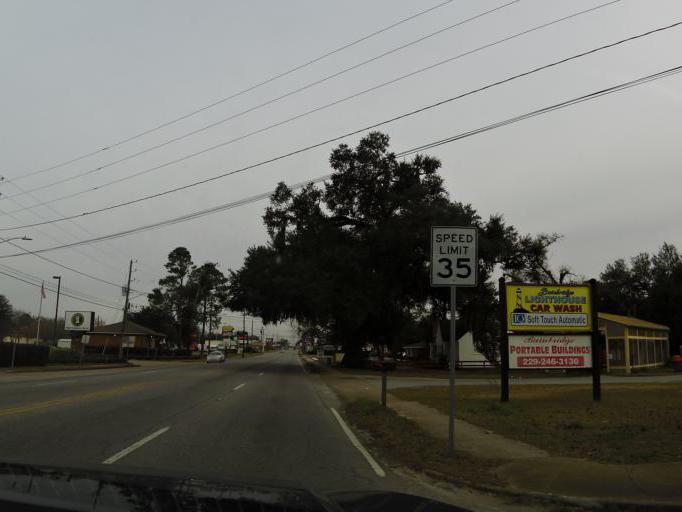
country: US
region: Georgia
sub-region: Decatur County
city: Bainbridge
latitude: 30.9039
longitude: -84.5673
